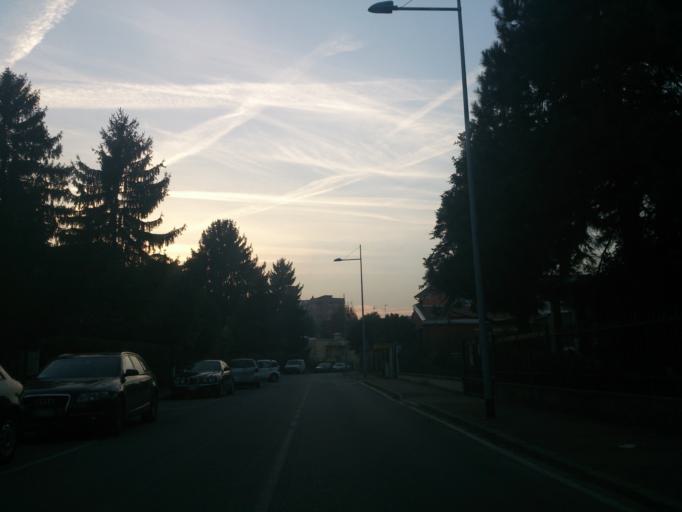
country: IT
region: Lombardy
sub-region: Citta metropolitana di Milano
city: San Donato Milanese
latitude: 45.4106
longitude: 9.2745
